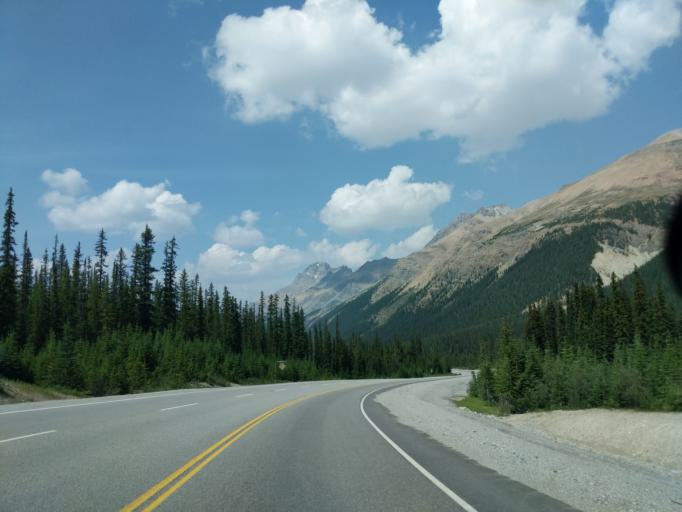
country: CA
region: Alberta
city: Lake Louise
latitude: 51.7254
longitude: -116.5009
